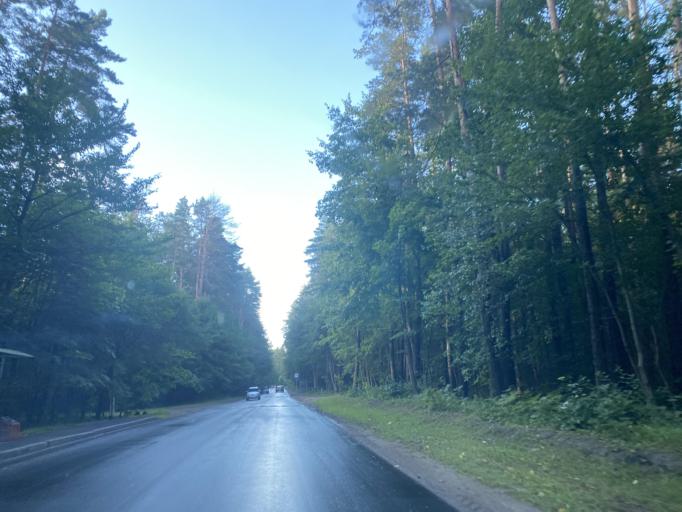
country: BY
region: Minsk
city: Borovlyany
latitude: 53.9202
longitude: 27.6540
